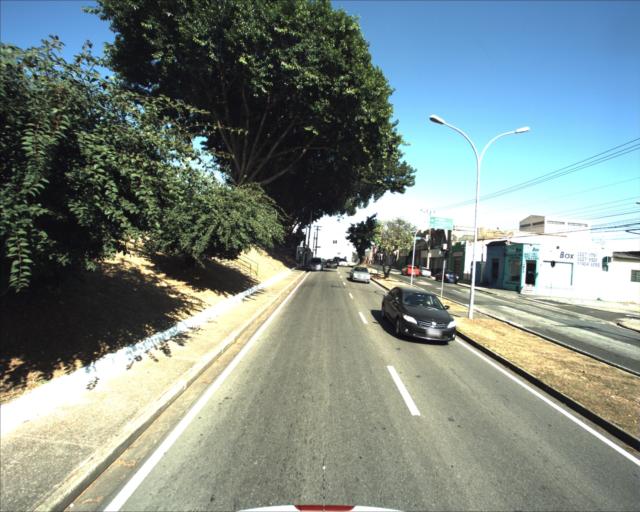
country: BR
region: Sao Paulo
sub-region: Sorocaba
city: Sorocaba
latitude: -23.4955
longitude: -47.4384
